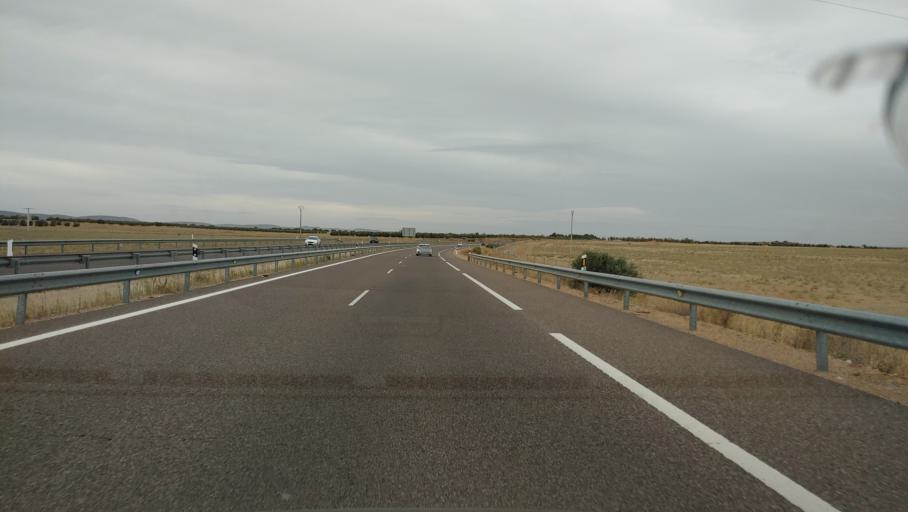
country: ES
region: Castille-La Mancha
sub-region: Provincia de Ciudad Real
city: Valenzuela de Calatrava
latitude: 38.8978
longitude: -3.8257
